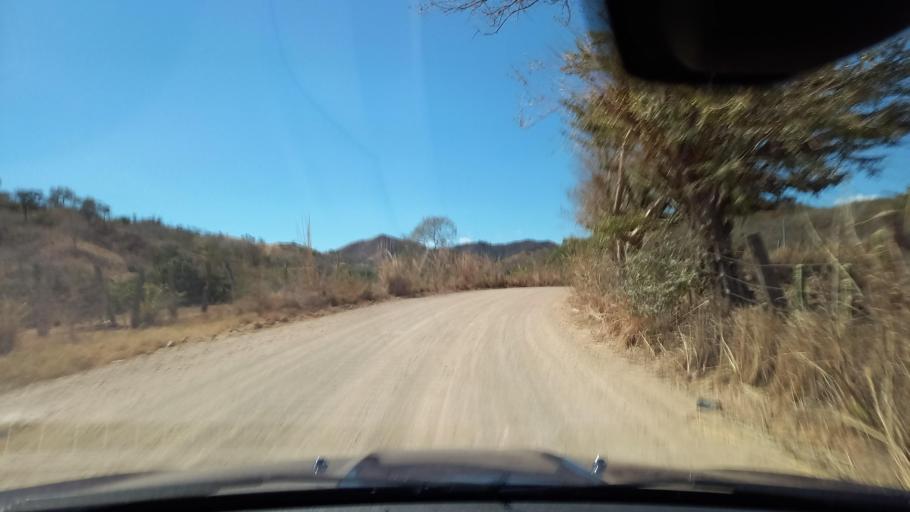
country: SV
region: Santa Ana
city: Metapan
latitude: 14.3604
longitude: -89.4638
